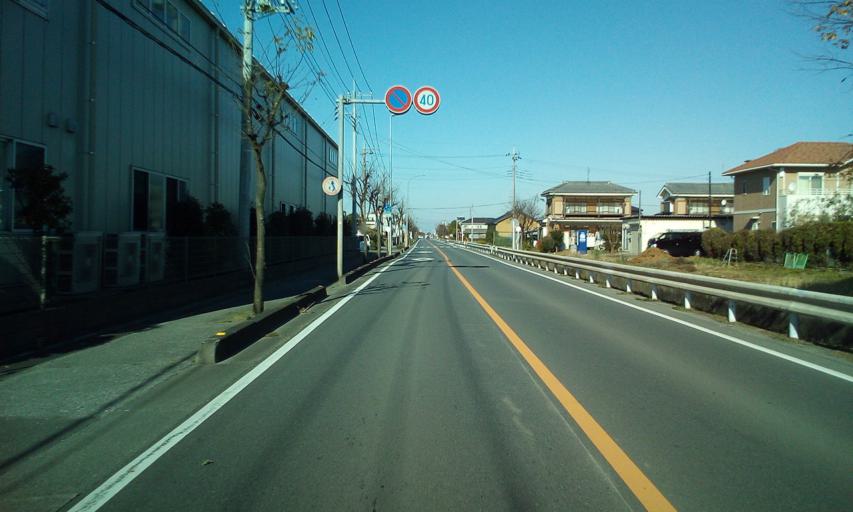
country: JP
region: Saitama
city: Kasukabe
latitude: 36.0058
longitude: 139.7947
